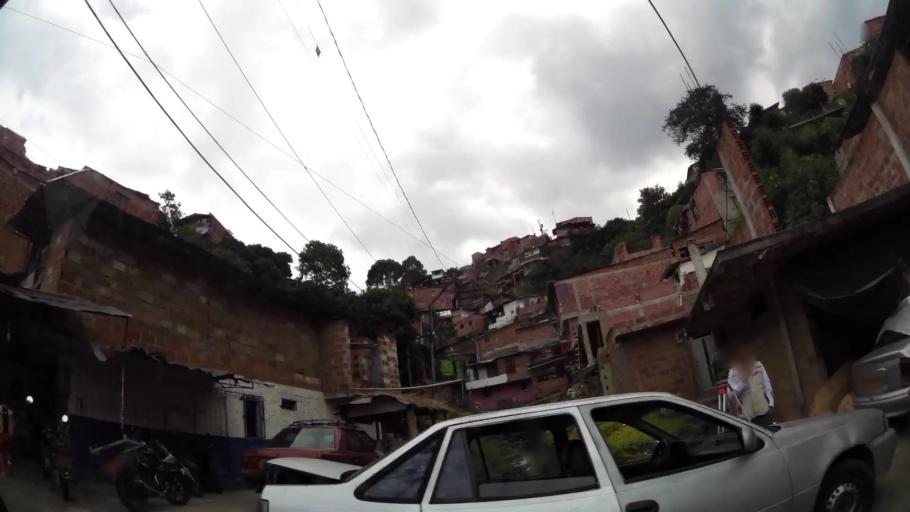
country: CO
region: Antioquia
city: Medellin
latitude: 6.2897
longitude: -75.5494
